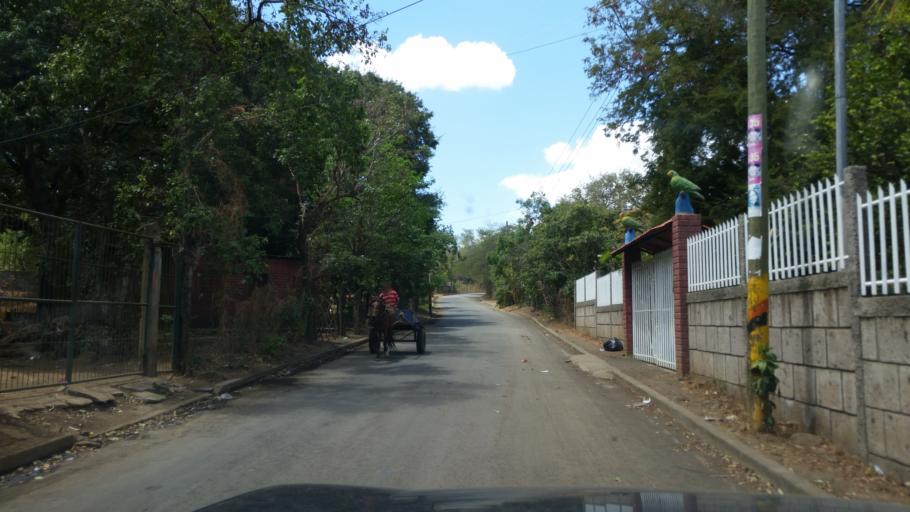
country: NI
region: Managua
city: Managua
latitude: 12.1068
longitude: -86.2177
